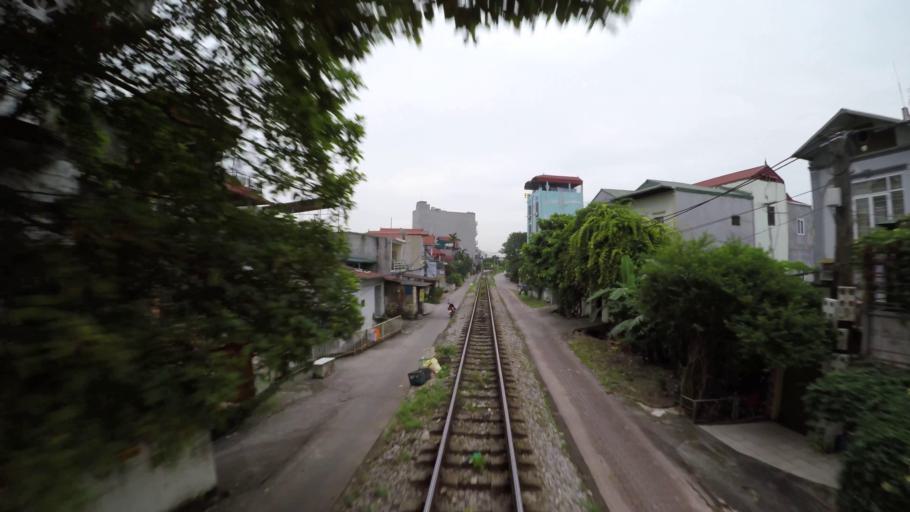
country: VN
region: Ha Noi
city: Trau Quy
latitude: 21.0210
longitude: 105.9376
